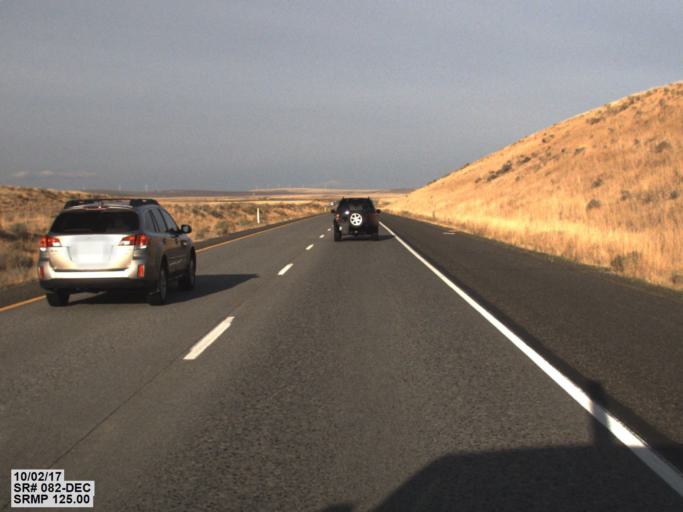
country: US
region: Oregon
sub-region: Umatilla County
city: Umatilla
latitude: 46.0019
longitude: -119.2530
